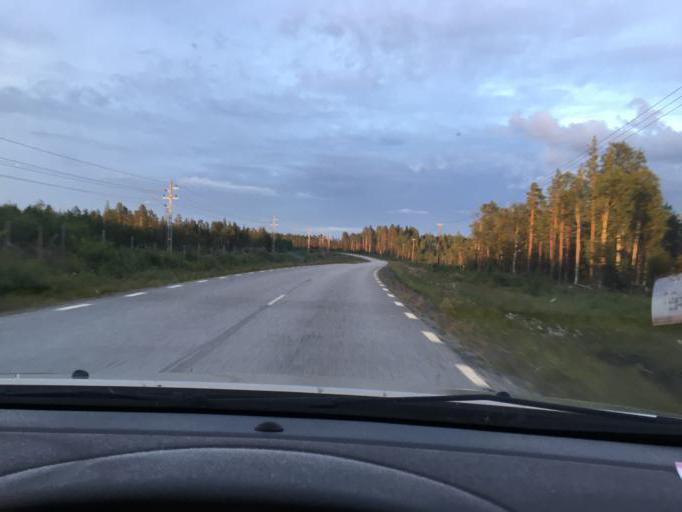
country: SE
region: Norrbotten
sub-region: Lulea Kommun
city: Ranea
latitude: 66.0403
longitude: 22.3193
